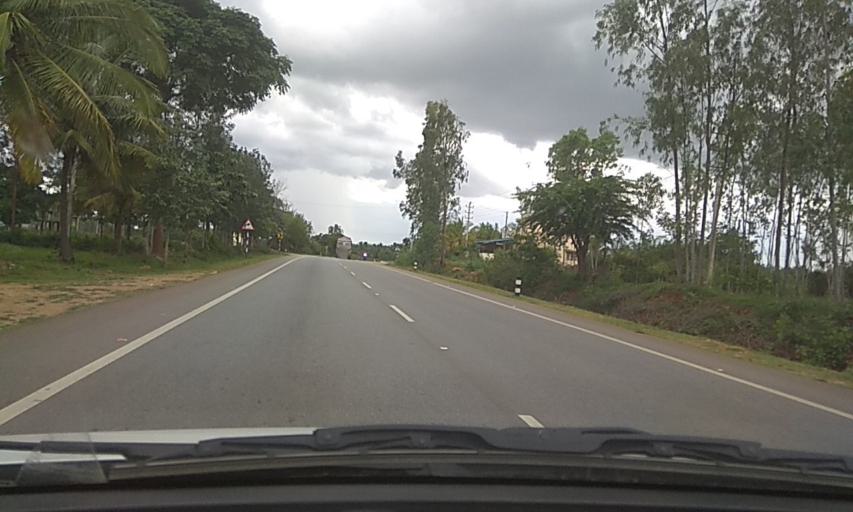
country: IN
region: Karnataka
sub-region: Tumkur
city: Gubbi
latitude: 13.1878
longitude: 77.0435
